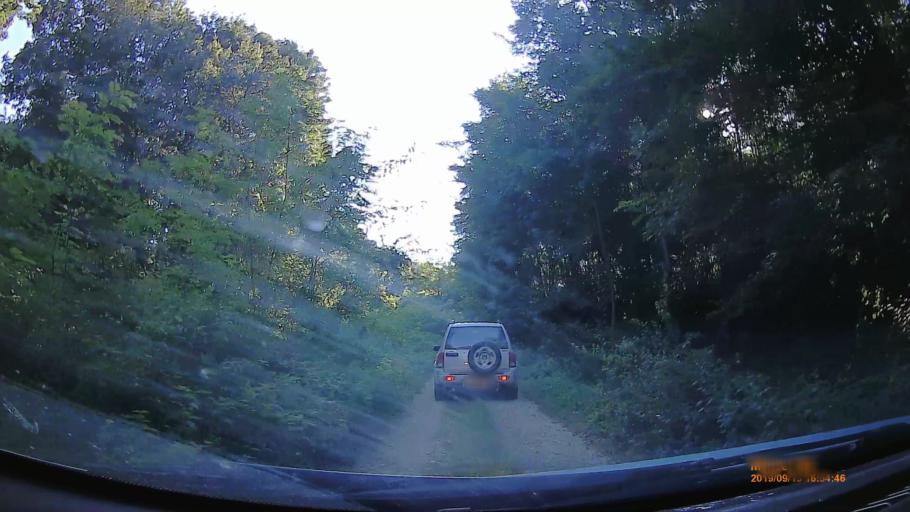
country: HU
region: Zala
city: Pacsa
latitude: 46.6010
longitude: 17.0581
